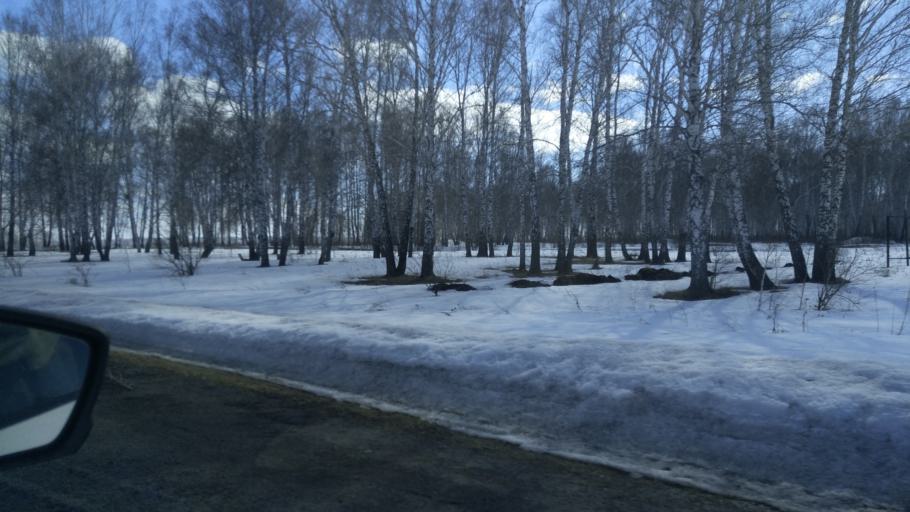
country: RU
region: Kemerovo
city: Yurga
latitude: 55.6857
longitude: 85.0750
